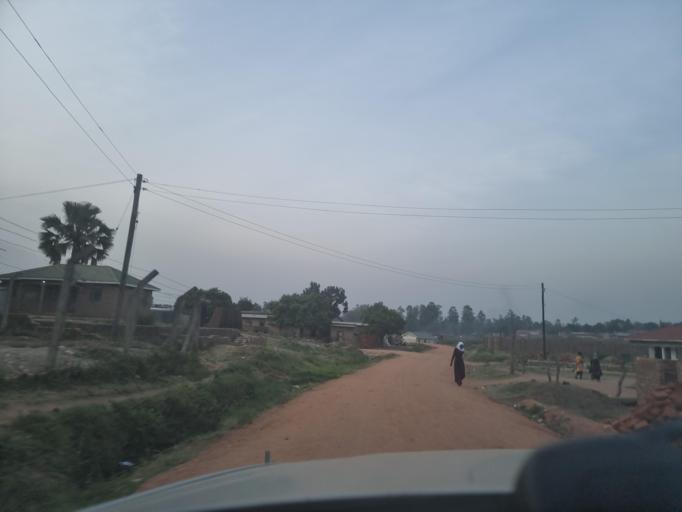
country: UG
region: Northern Region
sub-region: Arua District
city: Arua
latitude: 3.0338
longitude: 30.9108
